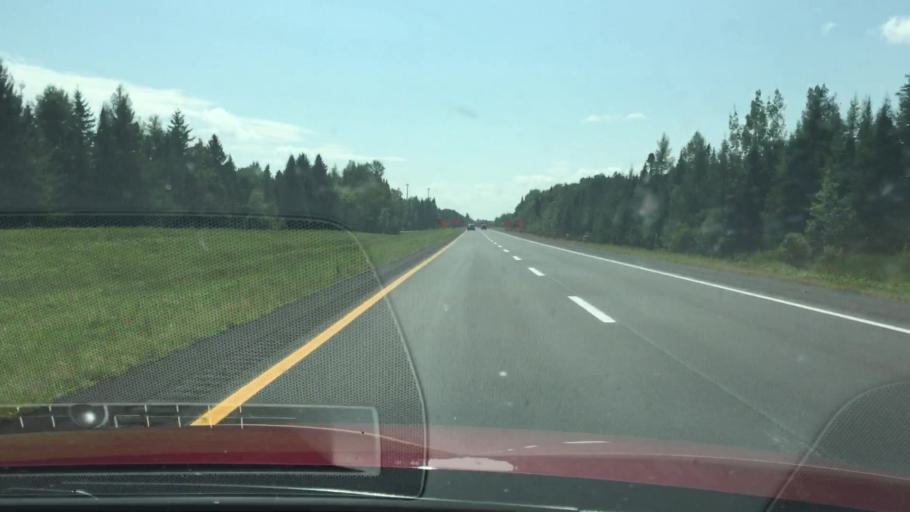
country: US
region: Maine
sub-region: Penobscot County
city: Patten
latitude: 45.8814
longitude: -68.4094
